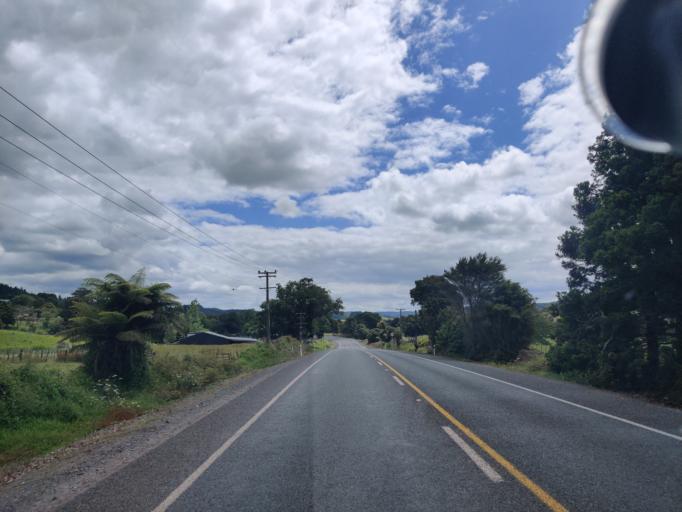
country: NZ
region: Northland
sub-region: Far North District
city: Kerikeri
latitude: -35.2941
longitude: 173.9750
